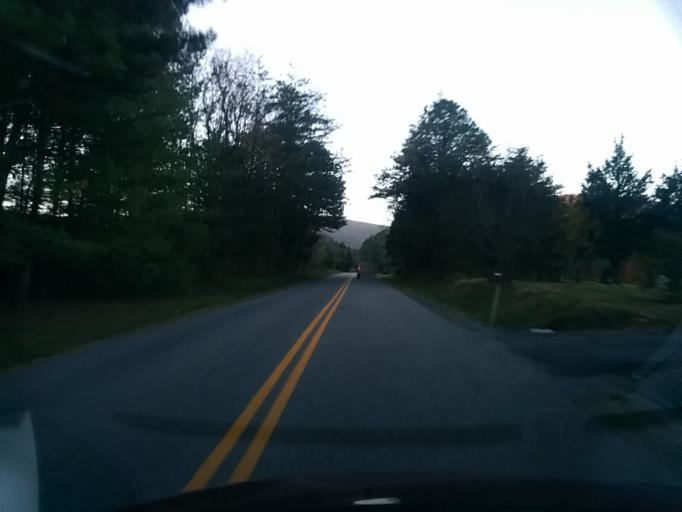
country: US
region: Virginia
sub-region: City of Lexington
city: Lexington
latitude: 37.9158
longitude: -79.5849
